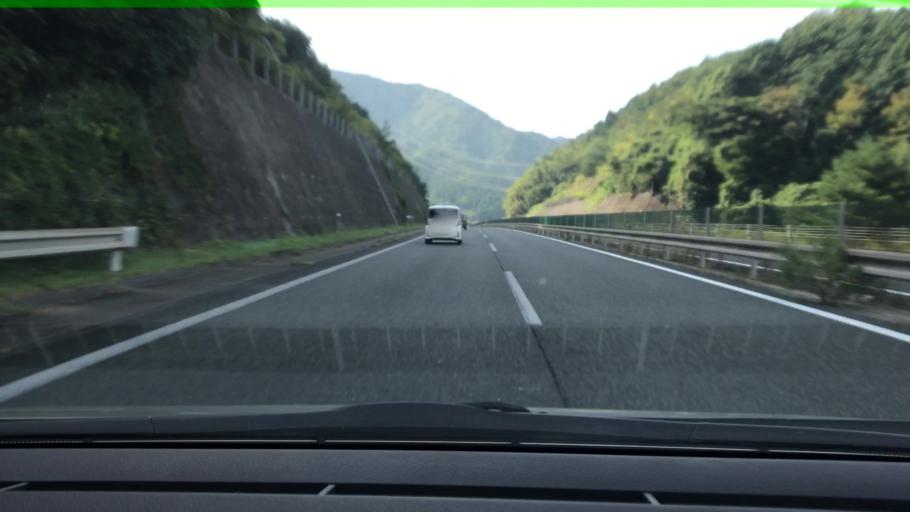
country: JP
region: Hyogo
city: Sasayama
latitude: 35.0429
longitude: 135.1824
